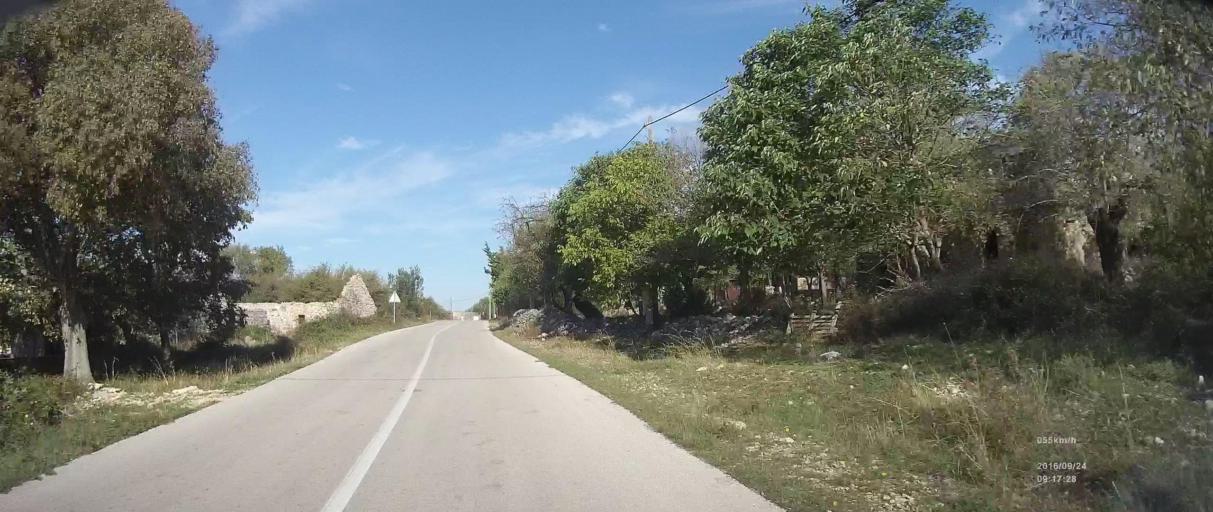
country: HR
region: Zadarska
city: Polaca
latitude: 44.0516
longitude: 15.5215
